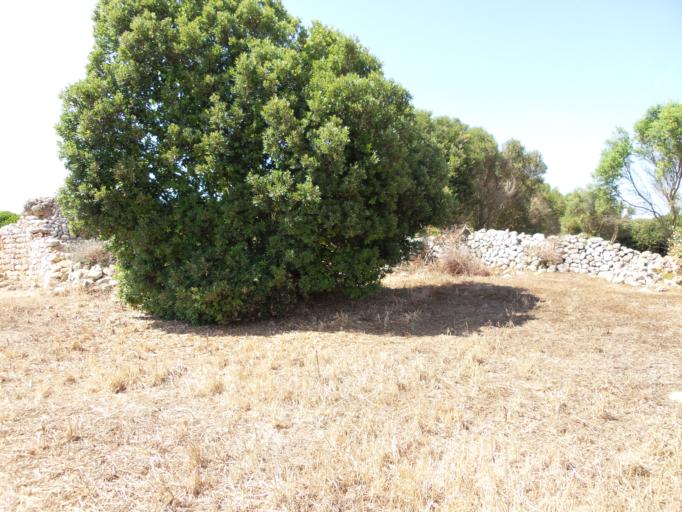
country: ES
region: Balearic Islands
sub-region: Illes Balears
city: Alaior
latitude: 39.9129
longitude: 4.1622
